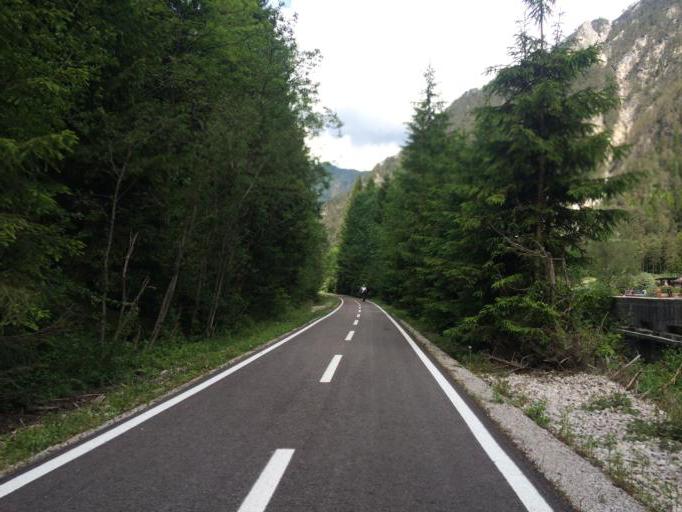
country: IT
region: Friuli Venezia Giulia
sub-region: Provincia di Udine
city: Malborghetto
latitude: 46.5068
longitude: 13.4913
